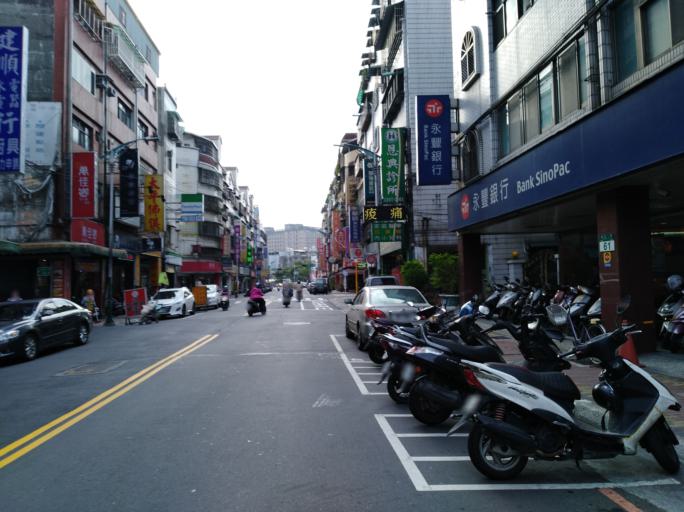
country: TW
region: Taipei
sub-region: Taipei
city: Banqiao
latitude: 25.0264
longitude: 121.4265
